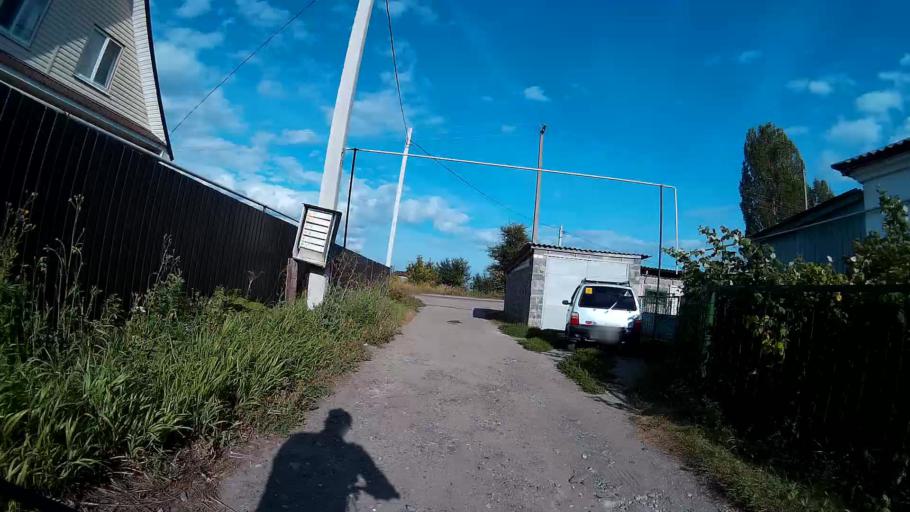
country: RU
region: Ulyanovsk
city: Isheyevka
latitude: 54.2894
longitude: 48.2008
